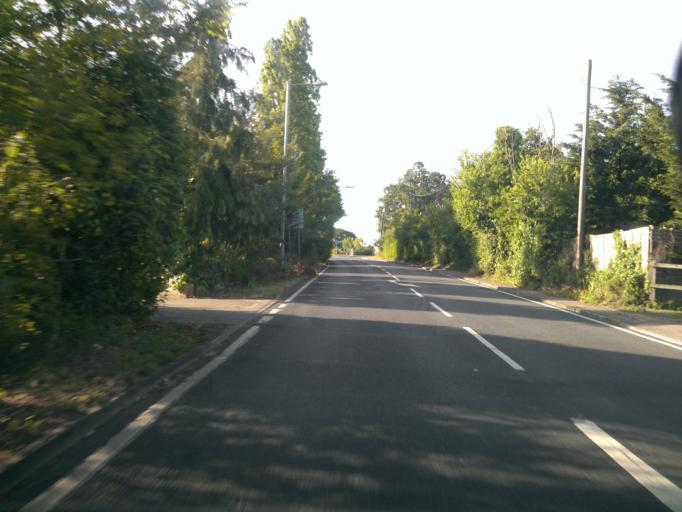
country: GB
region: England
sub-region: Essex
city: Little Clacton
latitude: 51.8186
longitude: 1.1417
